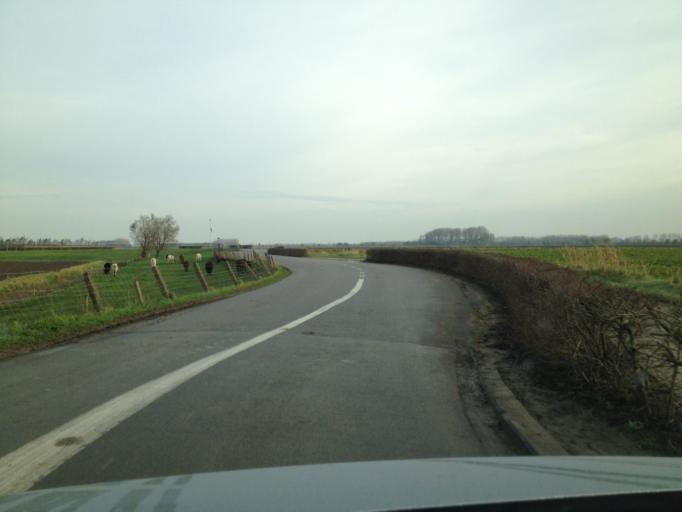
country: NL
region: Zeeland
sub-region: Gemeente Sluis
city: Sluis
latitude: 51.3348
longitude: 3.3583
